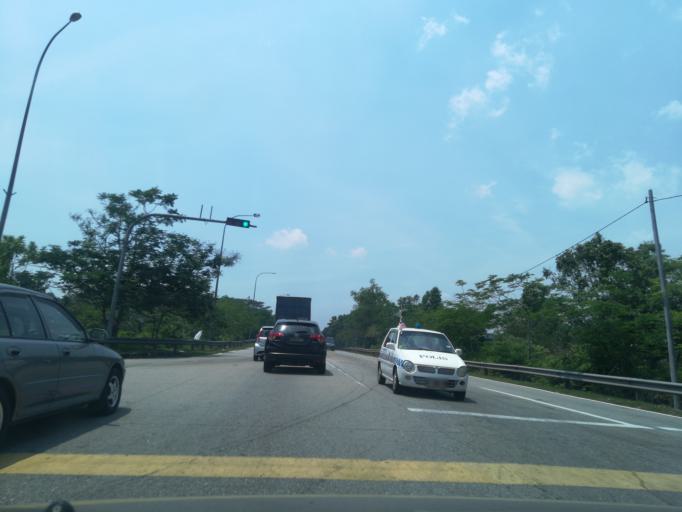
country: MY
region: Kedah
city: Kulim
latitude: 5.4251
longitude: 100.5652
